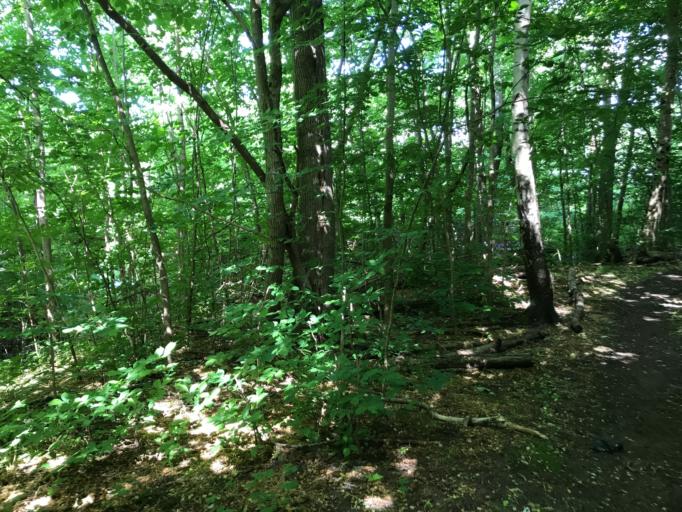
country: SE
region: Vaestra Goetaland
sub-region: Goteborg
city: Billdal
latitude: 57.5766
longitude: 11.9485
